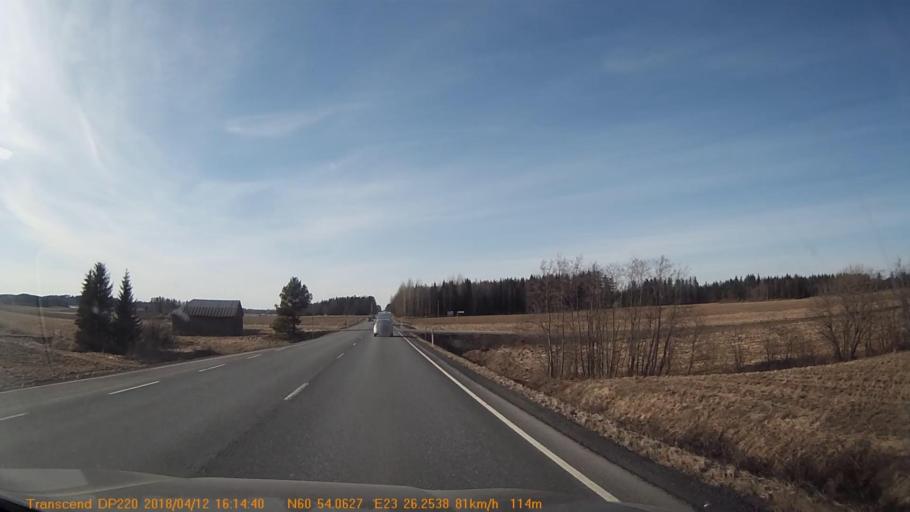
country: FI
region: Haeme
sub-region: Forssa
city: Humppila
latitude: 60.9011
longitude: 23.4374
